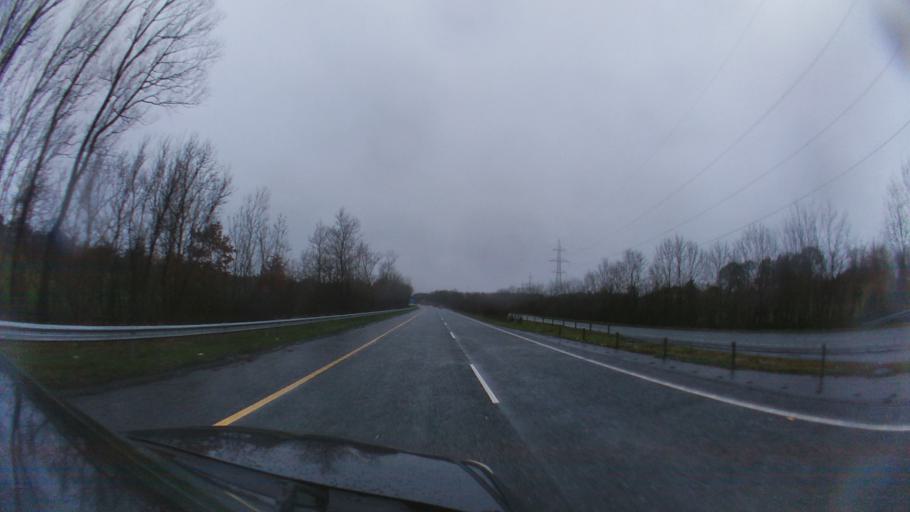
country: IE
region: Leinster
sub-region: Kildare
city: Kilcullen
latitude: 53.1433
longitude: -6.7610
